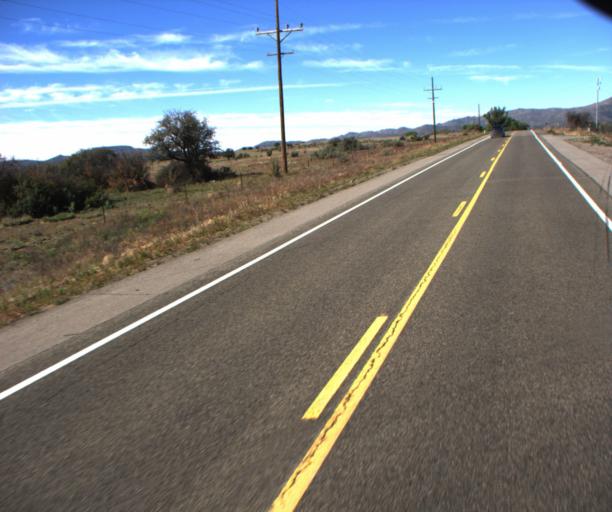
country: US
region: Arizona
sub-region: Yavapai County
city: Congress
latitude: 34.3040
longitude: -112.7177
